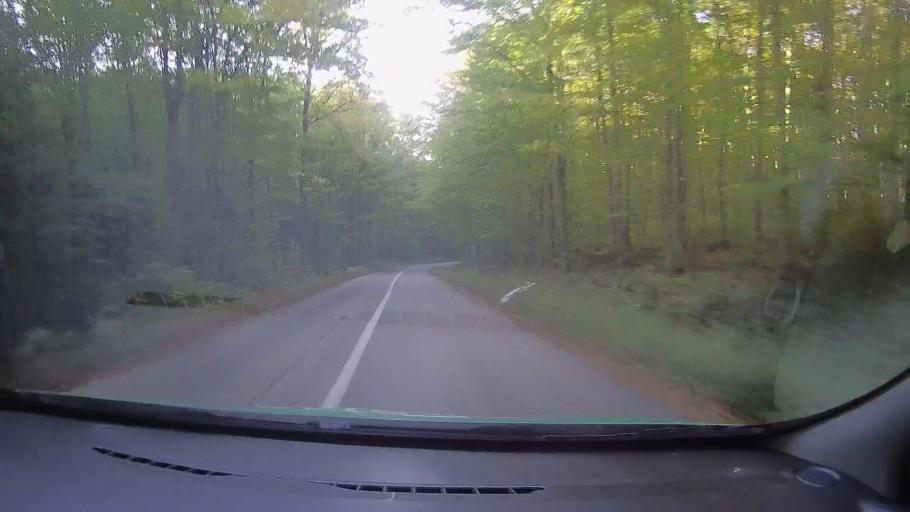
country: RO
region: Timis
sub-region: Comuna Nadrag
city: Nadrag
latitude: 45.6778
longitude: 22.1595
